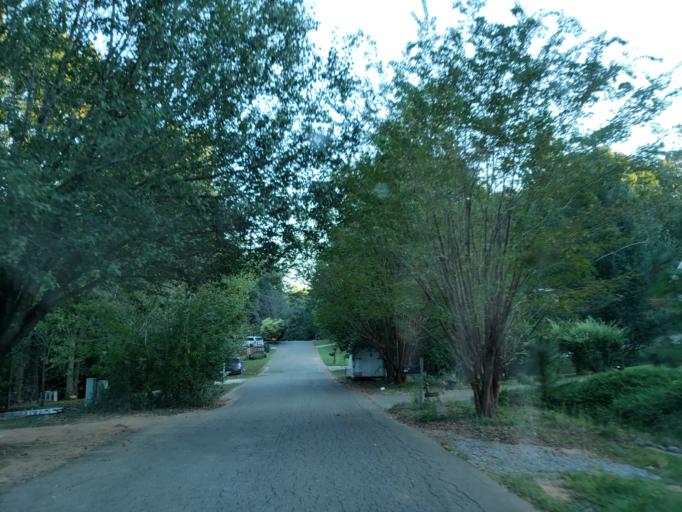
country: US
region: Georgia
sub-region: Pickens County
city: Jasper
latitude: 34.4275
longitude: -84.4348
